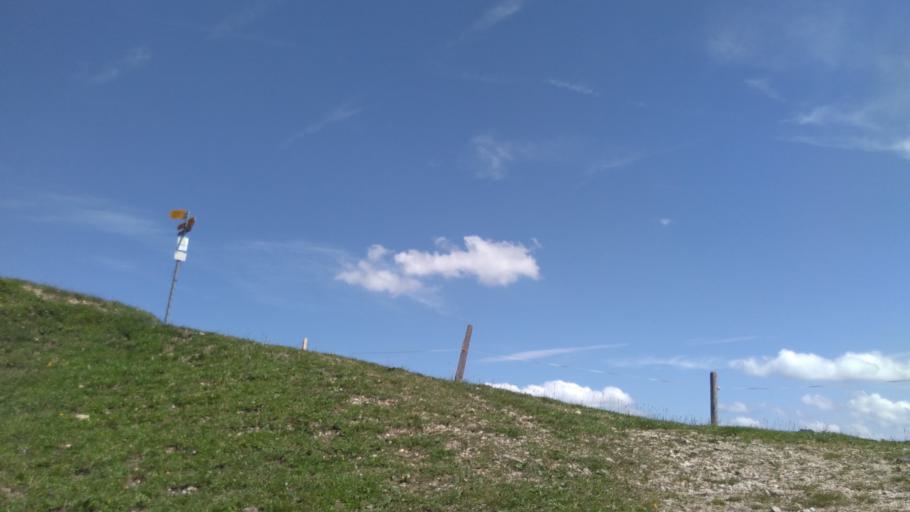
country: CH
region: Saint Gallen
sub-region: Wahlkreis See-Gaster
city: Goldingen
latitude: 47.2972
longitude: 9.0030
